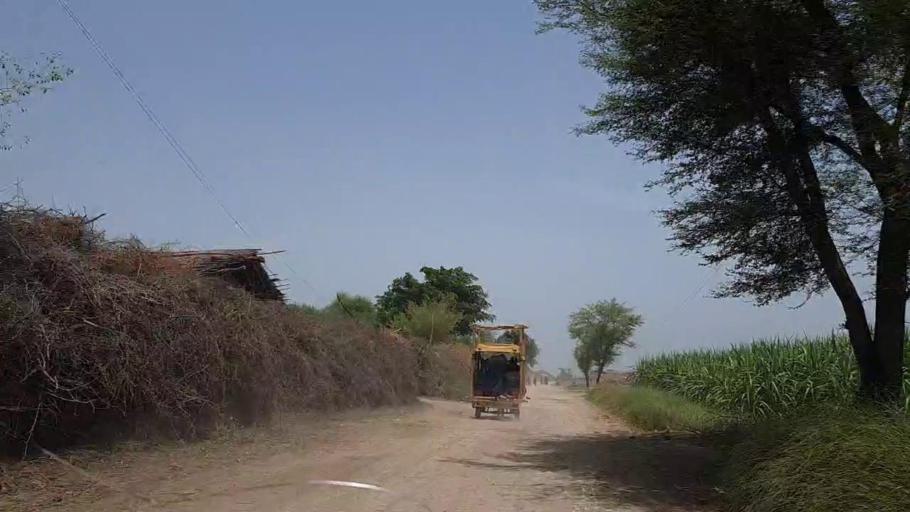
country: PK
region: Sindh
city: Tharu Shah
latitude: 26.9056
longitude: 68.0057
